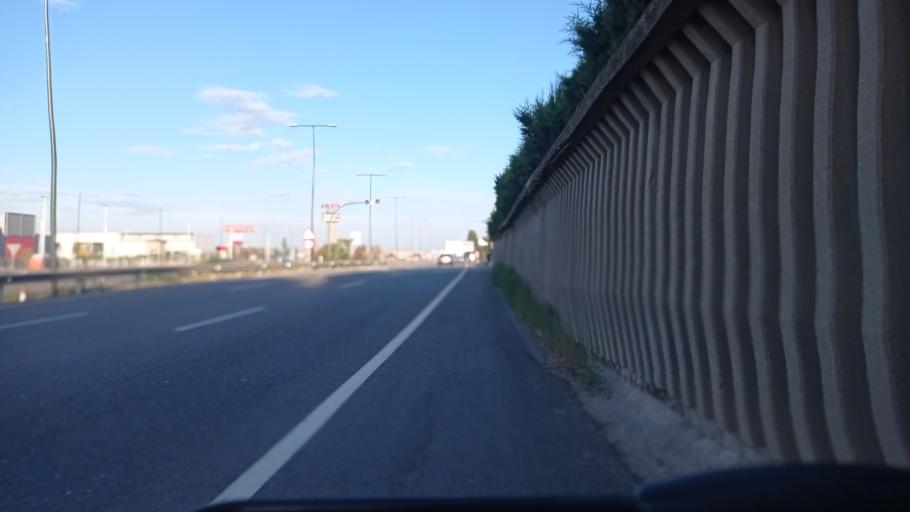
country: ES
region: Aragon
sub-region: Provincia de Zaragoza
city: Oliver-Valdefierro, Oliver, Valdefierro
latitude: 41.6759
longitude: -0.9569
